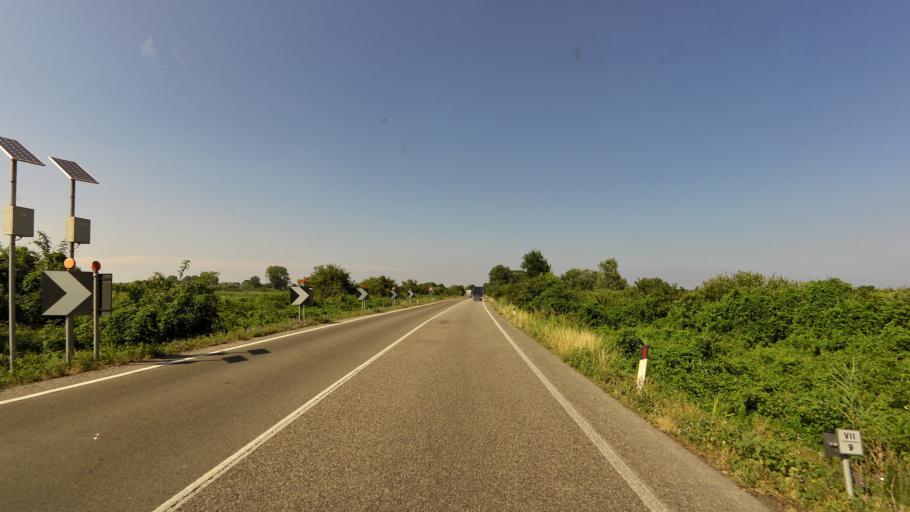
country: IT
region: Emilia-Romagna
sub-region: Provincia di Ravenna
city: Marina Romea
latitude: 44.5407
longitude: 12.2349
